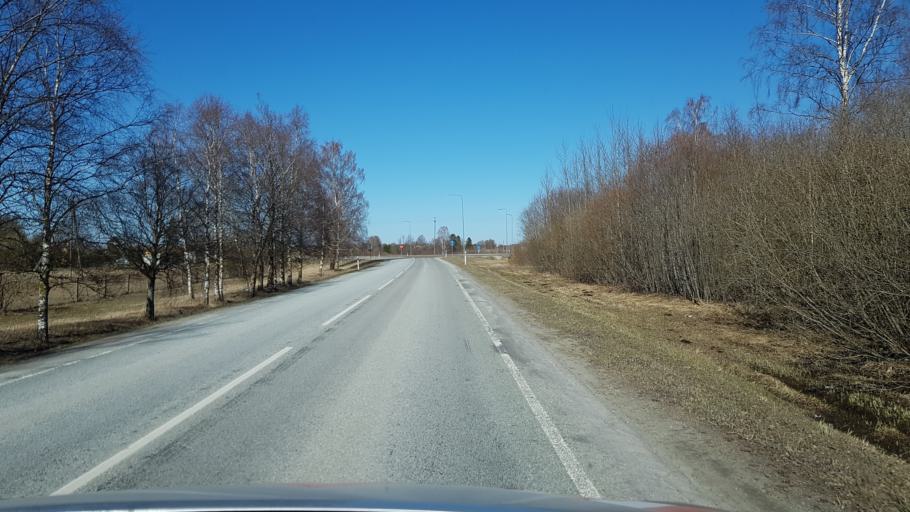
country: EE
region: Laeaene-Virumaa
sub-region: Someru vald
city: Someru
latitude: 59.3874
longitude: 26.3939
